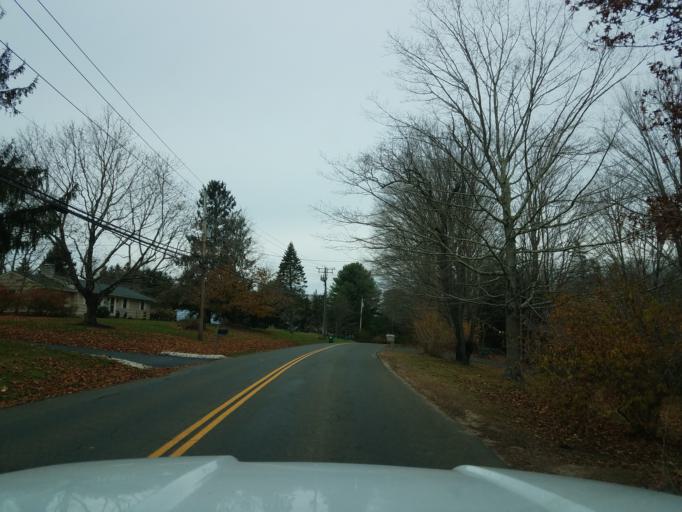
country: US
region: Connecticut
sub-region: New Haven County
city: Guilford
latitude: 41.3147
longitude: -72.7083
